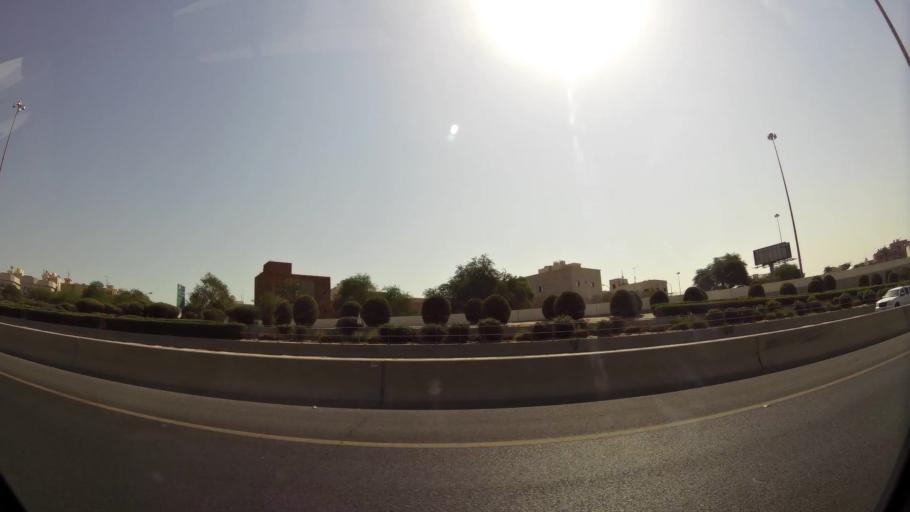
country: KW
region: Al Asimah
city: Ad Dasmah
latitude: 29.3657
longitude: 47.9930
